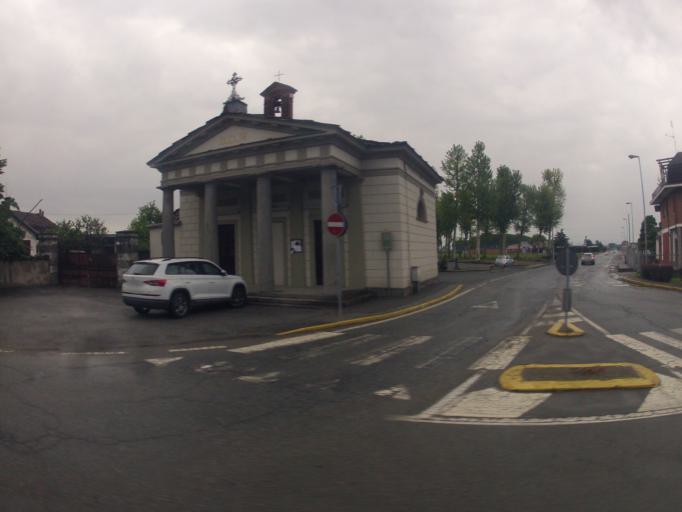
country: IT
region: Piedmont
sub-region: Provincia di Cuneo
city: Moretta
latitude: 44.7622
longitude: 7.5420
